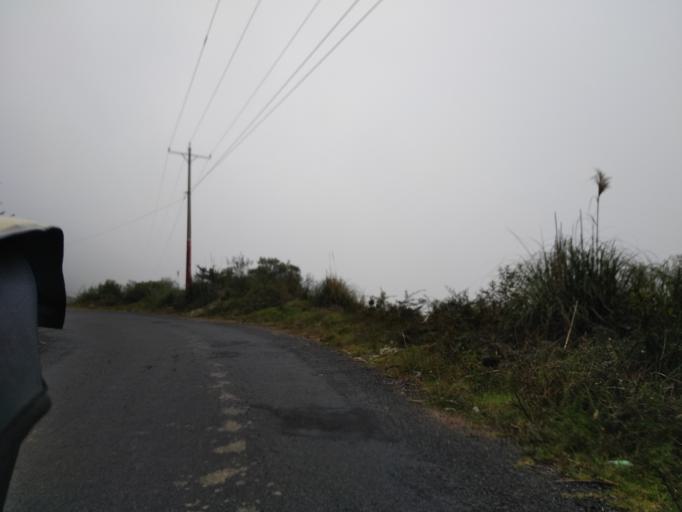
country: EC
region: Cotopaxi
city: Saquisili
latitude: -0.6874
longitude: -78.8315
